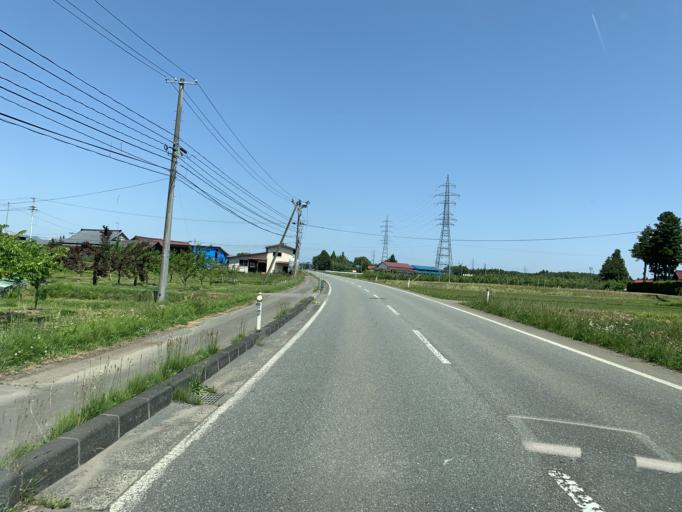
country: JP
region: Iwate
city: Mizusawa
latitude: 39.1765
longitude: 141.0813
